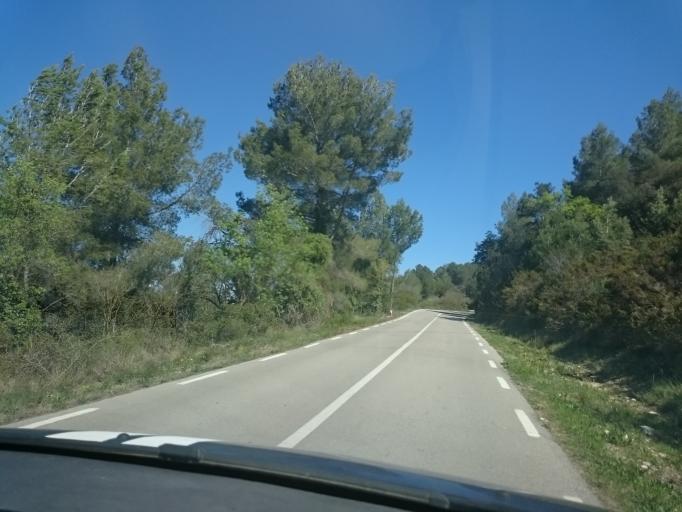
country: ES
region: Catalonia
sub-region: Provincia de Barcelona
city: Castellet
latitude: 41.2667
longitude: 1.6374
